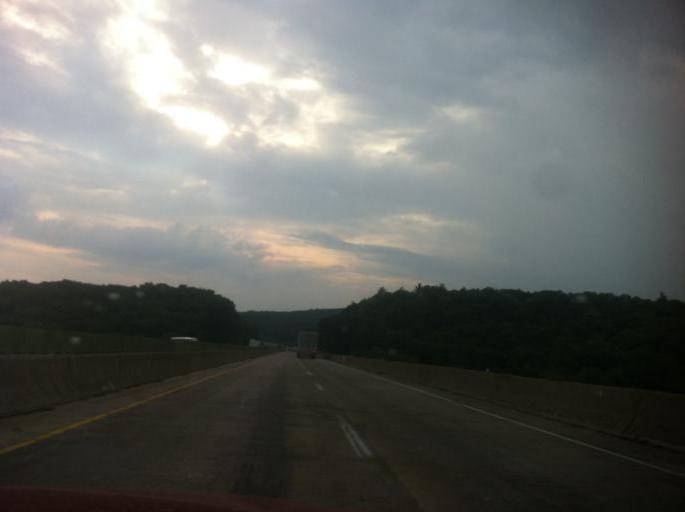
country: US
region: Pennsylvania
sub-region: Clarion County
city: Marianne
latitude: 41.1961
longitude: -79.4582
